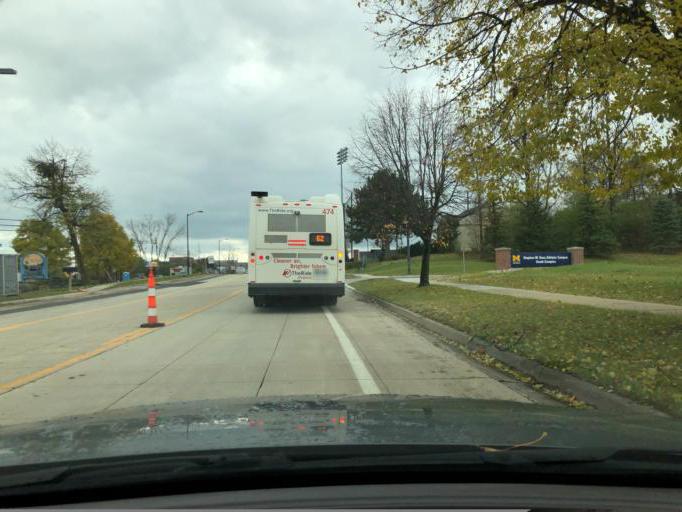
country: US
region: Michigan
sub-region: Washtenaw County
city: Ann Arbor
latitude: 42.2531
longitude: -83.7397
